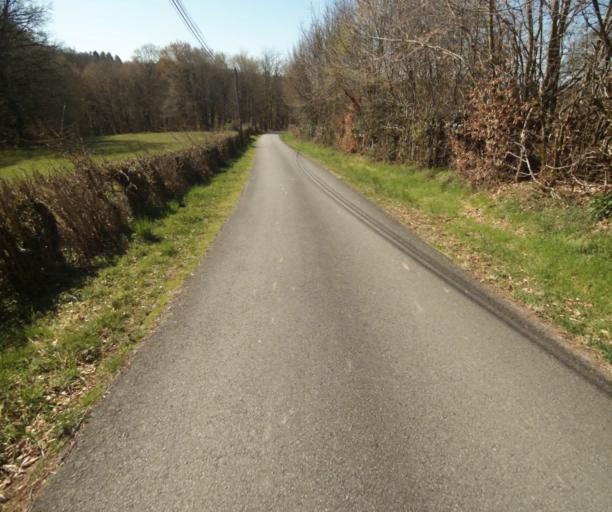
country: FR
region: Limousin
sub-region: Departement de la Correze
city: Saint-Mexant
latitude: 45.3082
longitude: 1.6346
